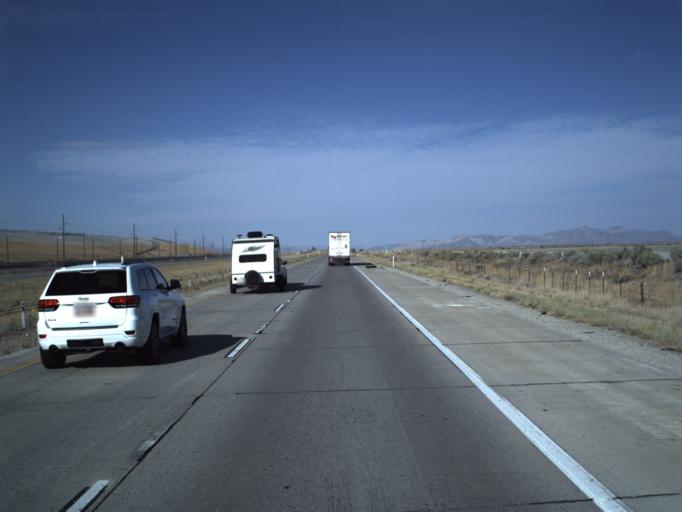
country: US
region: Utah
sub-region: Salt Lake County
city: Magna
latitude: 40.7710
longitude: -112.1238
